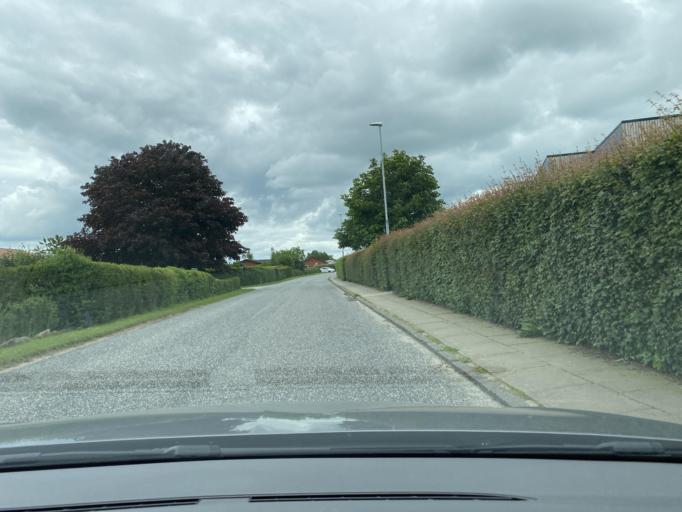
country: DK
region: South Denmark
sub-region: Vejle Kommune
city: Vejle
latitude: 55.6581
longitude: 9.4971
